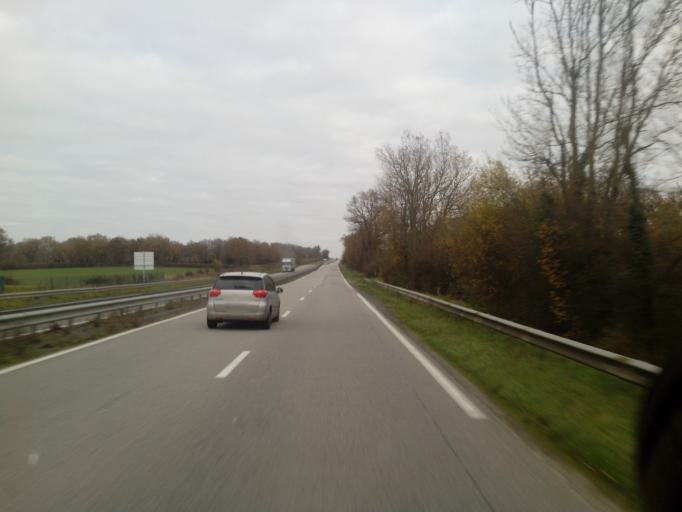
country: FR
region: Poitou-Charentes
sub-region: Departement des Deux-Sevres
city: La Peyratte
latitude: 46.6515
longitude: -0.1391
